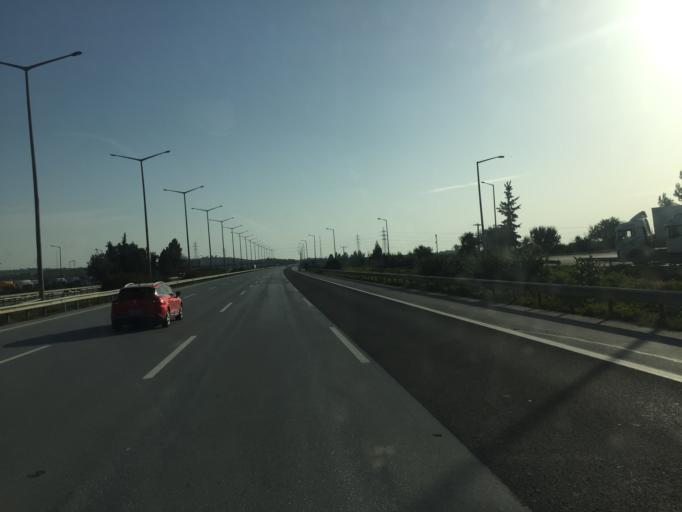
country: TR
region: Mersin
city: Yenice
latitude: 37.0236
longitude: 35.0627
